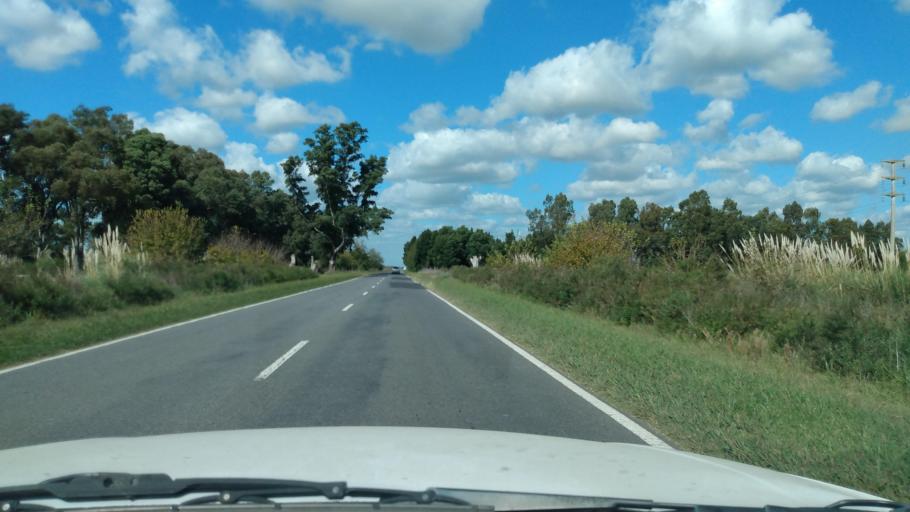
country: AR
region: Buenos Aires
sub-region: Partido de Navarro
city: Navarro
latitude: -34.8855
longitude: -59.3394
